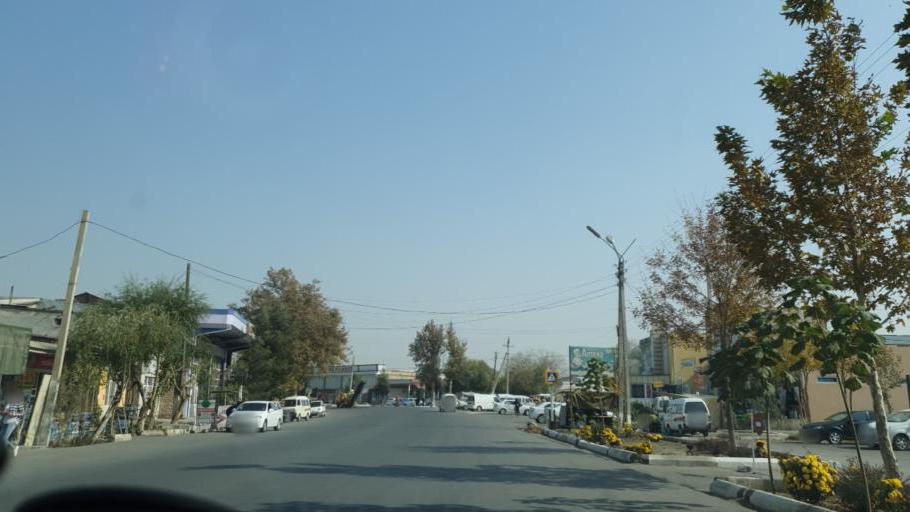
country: UZ
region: Fergana
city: Beshariq
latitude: 40.4361
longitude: 70.6016
